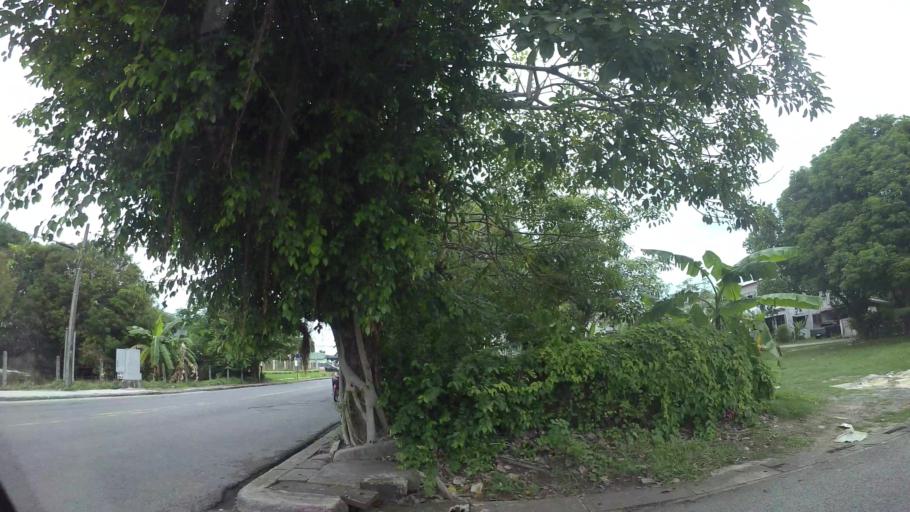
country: TH
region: Rayong
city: Rayong
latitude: 12.6726
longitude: 101.2766
